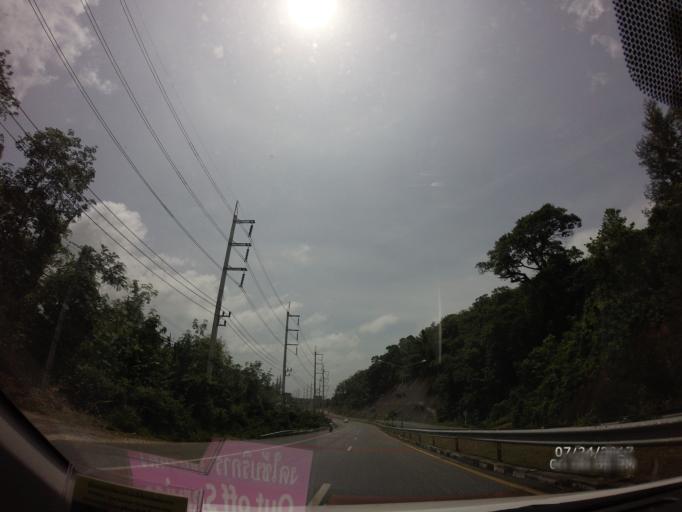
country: TH
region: Phuket
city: Thalang
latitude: 8.0896
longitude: 98.3170
